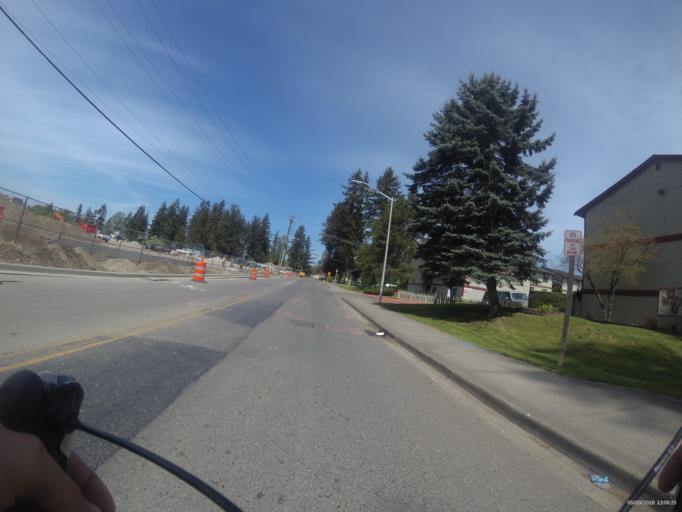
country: US
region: Washington
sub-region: Pierce County
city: McChord Air Force Base
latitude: 47.1416
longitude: -122.5019
